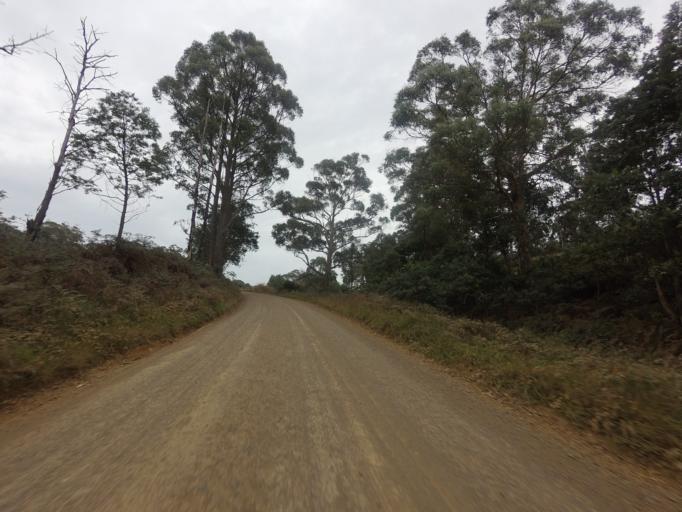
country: AU
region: Tasmania
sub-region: Derwent Valley
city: New Norfolk
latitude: -42.5803
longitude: 147.0065
